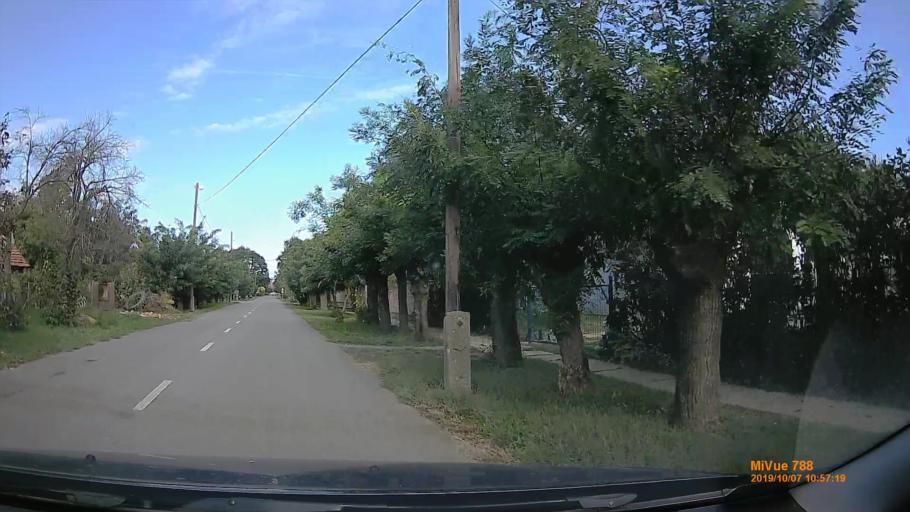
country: HU
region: Bekes
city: Kondoros
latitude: 46.7537
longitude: 20.7989
